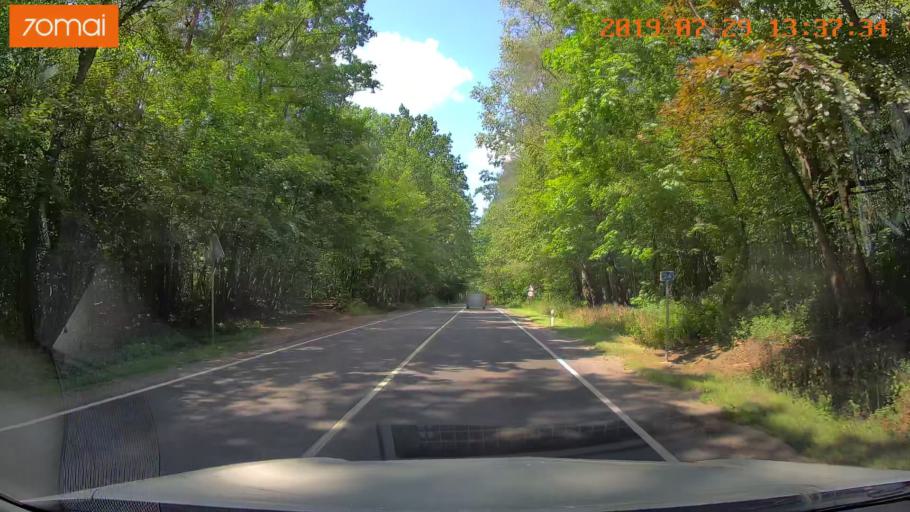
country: RU
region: Kaliningrad
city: Volochayevskoye
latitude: 54.7152
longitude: 20.1823
